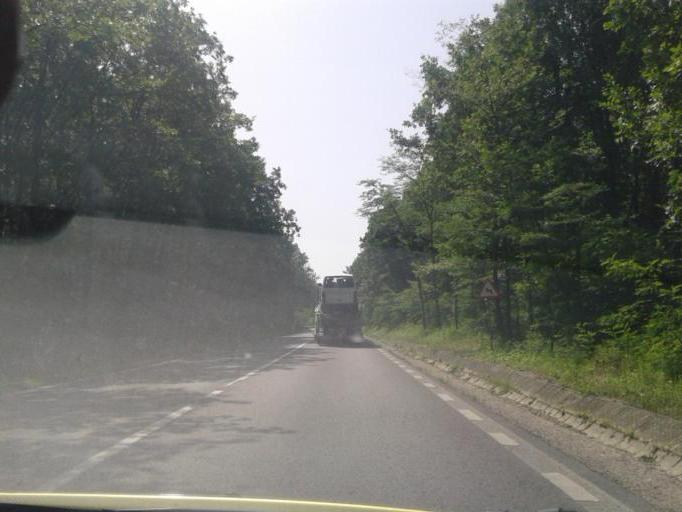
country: RO
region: Arges
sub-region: Comuna Cotmeana
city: Cotmeana
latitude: 44.9803
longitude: 24.6571
